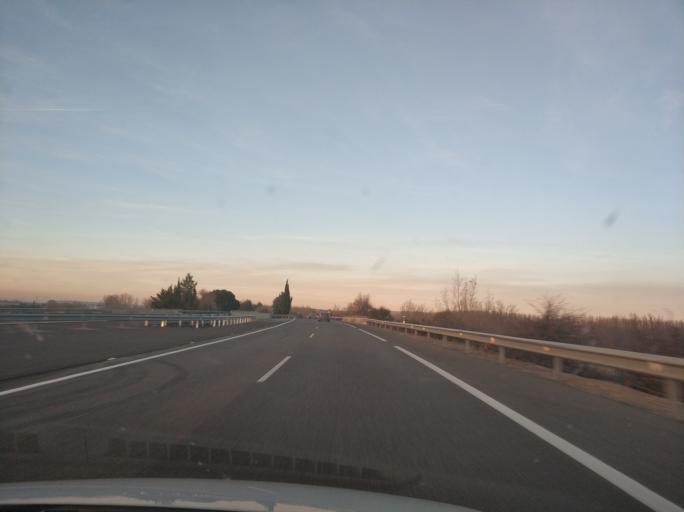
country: ES
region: Castille and Leon
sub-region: Provincia de Palencia
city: Venta de Banos
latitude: 41.9294
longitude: -4.4985
